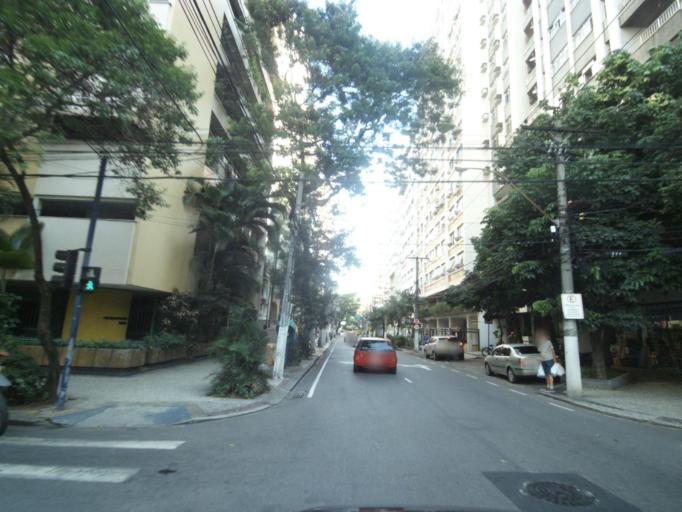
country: BR
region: Rio de Janeiro
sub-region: Niteroi
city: Niteroi
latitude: -22.9019
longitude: -43.1103
